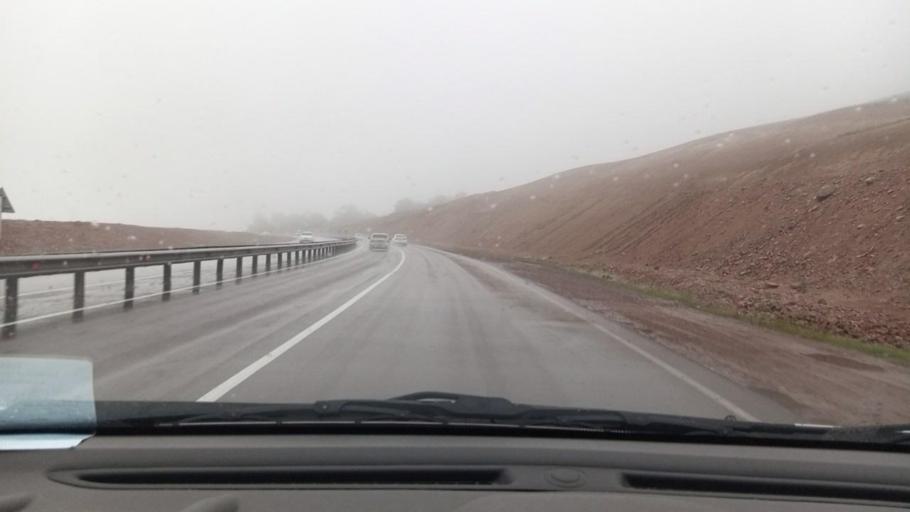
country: UZ
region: Toshkent
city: Angren
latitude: 41.0613
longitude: 70.1816
